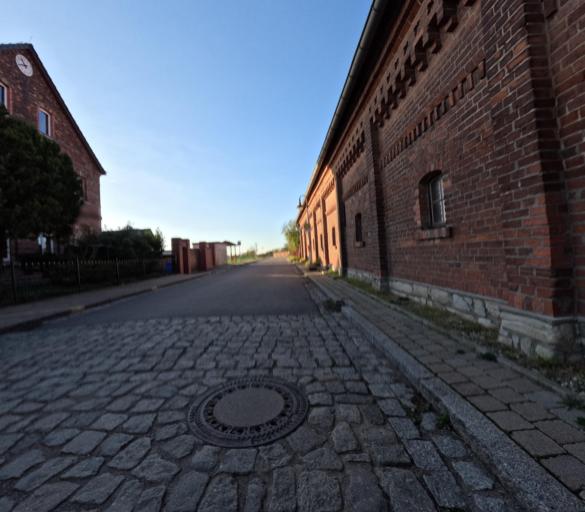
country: DE
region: Saxony-Anhalt
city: Gunthersdorf
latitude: 51.3563
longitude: 12.1845
